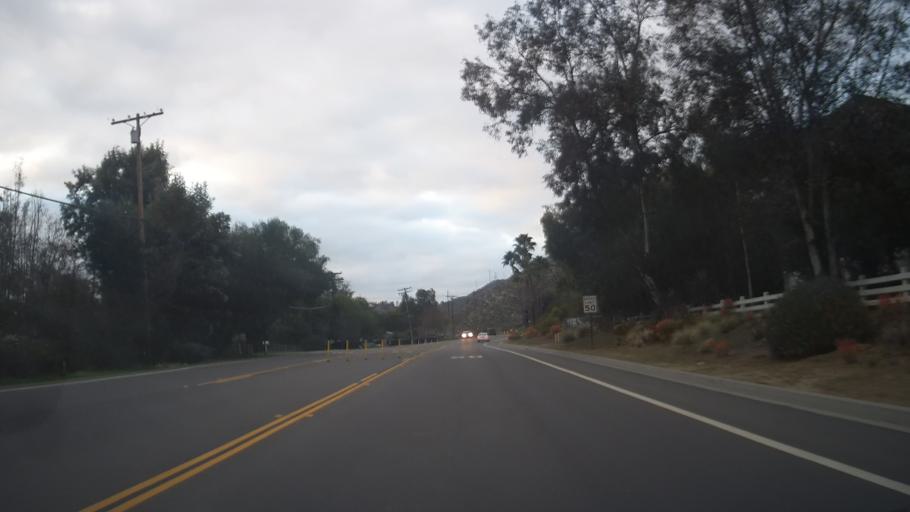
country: US
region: California
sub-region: San Diego County
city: Crest
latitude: 32.7811
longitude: -116.8739
